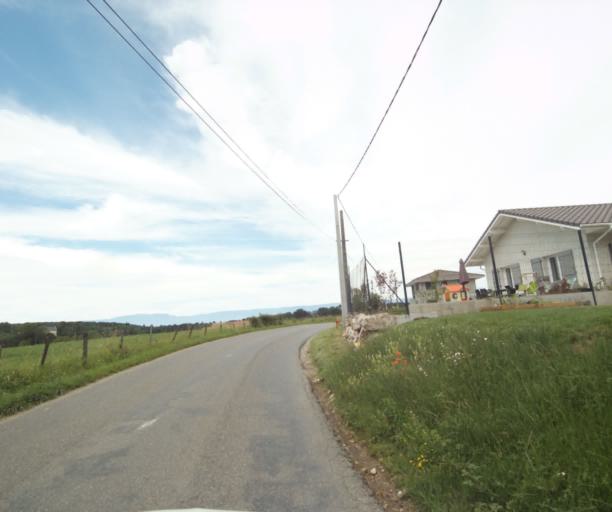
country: FR
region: Rhone-Alpes
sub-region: Departement de la Haute-Savoie
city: Allinges
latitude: 46.3418
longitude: 6.4581
